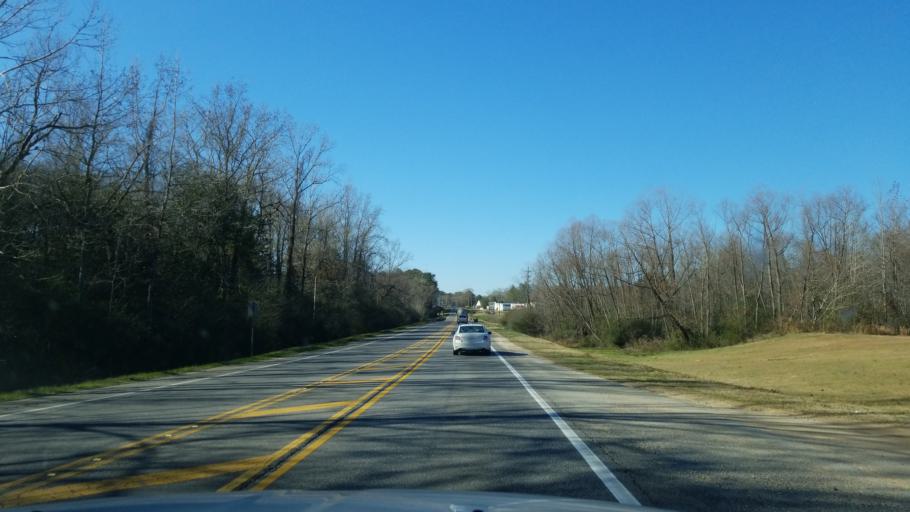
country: US
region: Alabama
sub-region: Pickens County
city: Gordo
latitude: 33.3141
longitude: -87.8960
